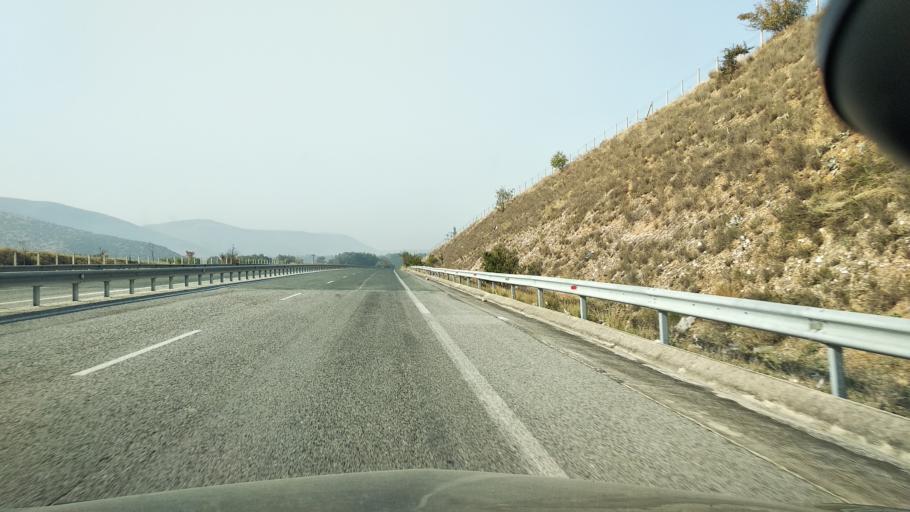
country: GR
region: Thessaly
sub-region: Trikala
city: Zarkos
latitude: 39.5916
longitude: 22.1703
